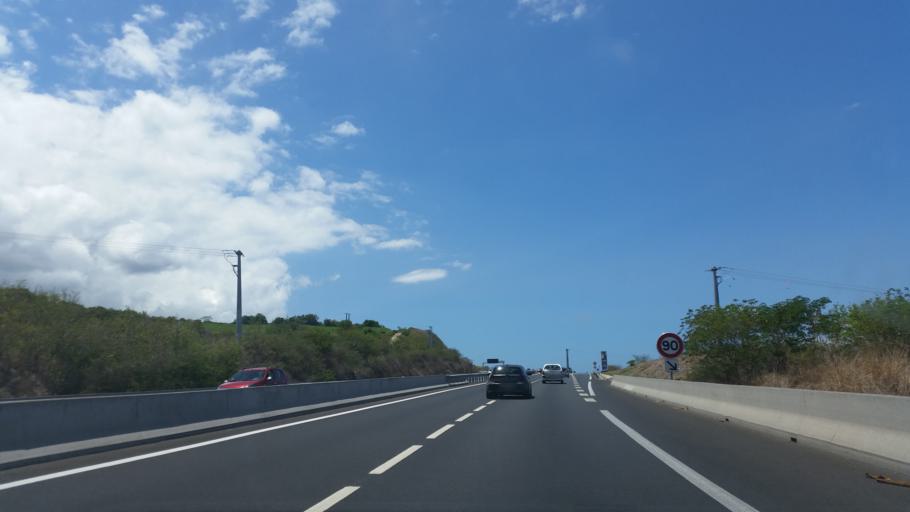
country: RE
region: Reunion
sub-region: Reunion
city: Trois-Bassins
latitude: -21.0841
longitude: 55.2560
